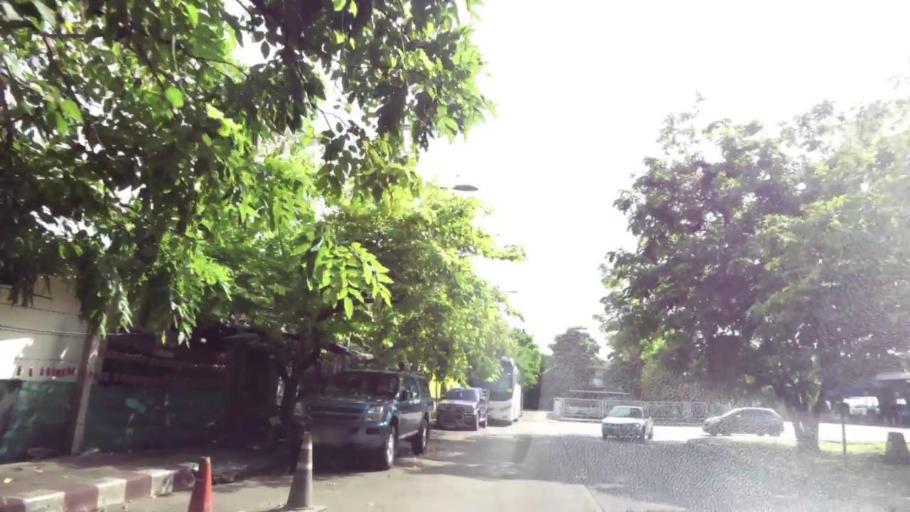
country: TH
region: Bangkok
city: Phra Khanong
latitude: 13.7156
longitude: 100.6005
